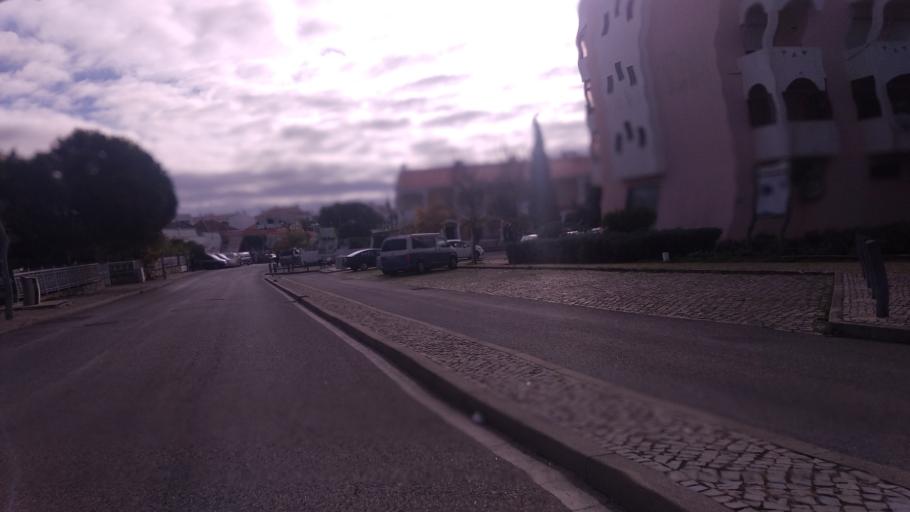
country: PT
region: Faro
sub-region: Sao Bras de Alportel
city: Sao Bras de Alportel
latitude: 37.1574
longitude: -7.8933
